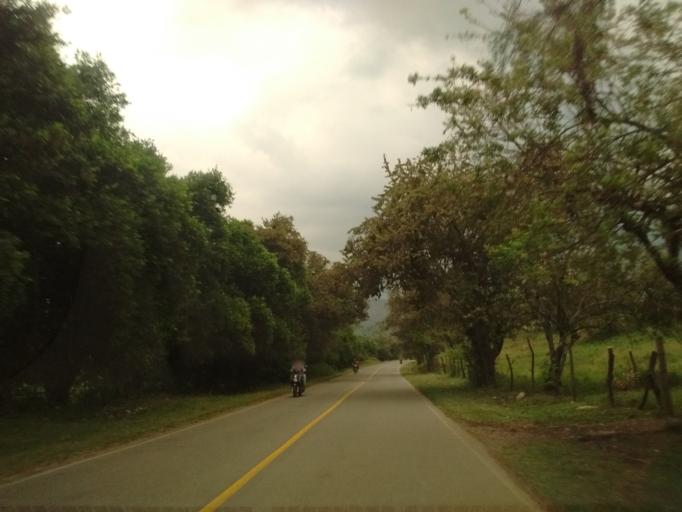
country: CO
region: Cauca
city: Caloto
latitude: 3.0654
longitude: -76.3632
